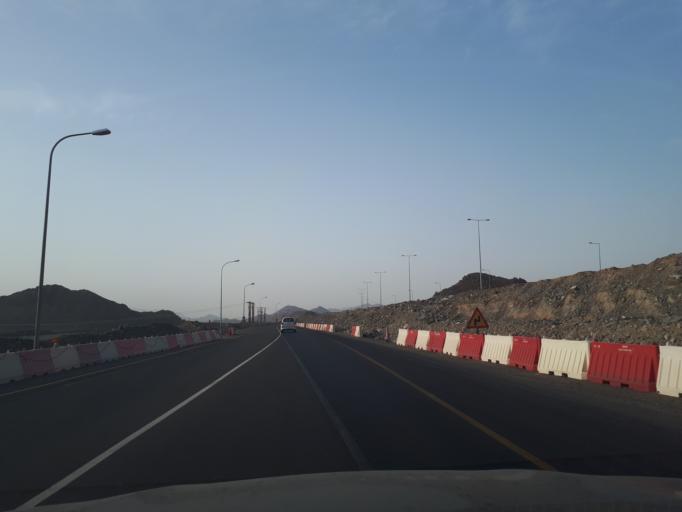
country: OM
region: Muhafazat ad Dakhiliyah
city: Sufalat Sama'il
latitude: 23.2687
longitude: 58.1044
